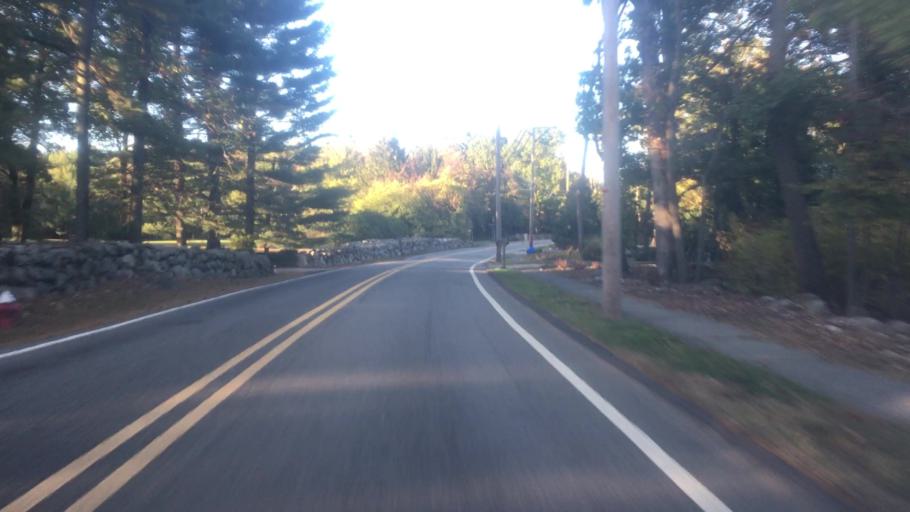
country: US
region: New Jersey
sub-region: Bergen County
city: Franklin Lakes
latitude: 40.9902
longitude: -74.1999
